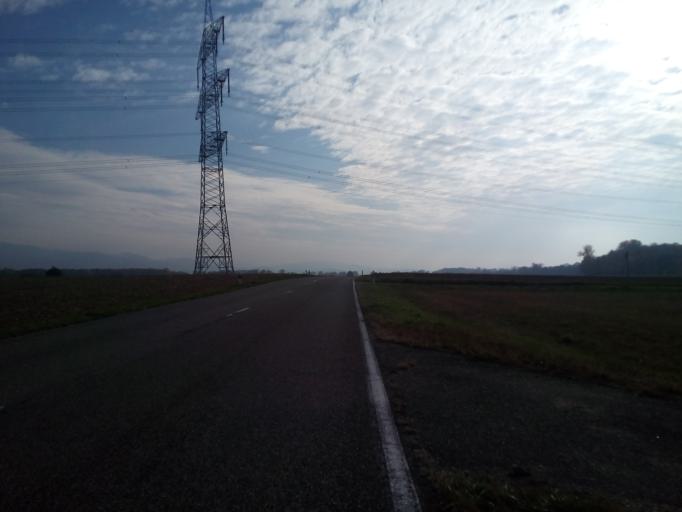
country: DE
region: Baden-Wuerttemberg
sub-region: Karlsruhe Region
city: Zell
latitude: 48.7096
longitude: 8.0686
